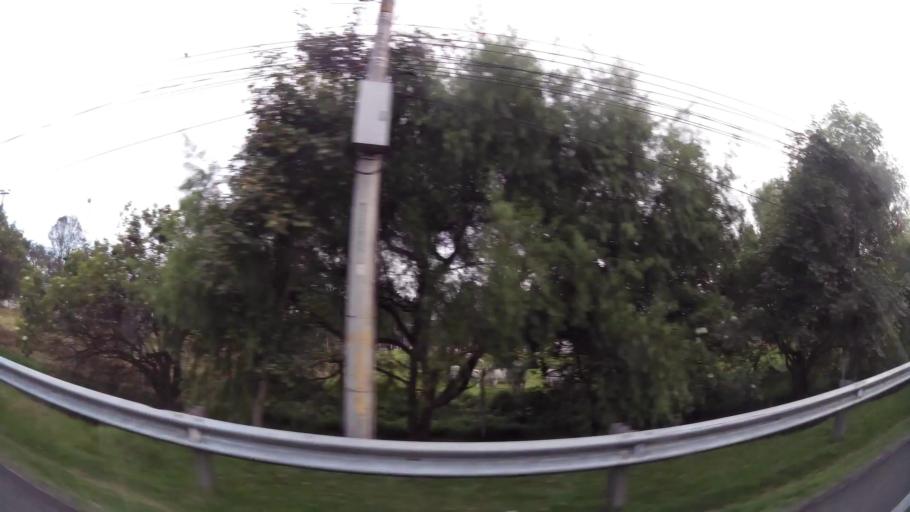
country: CO
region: Cundinamarca
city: Funza
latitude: 4.6975
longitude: -74.2050
